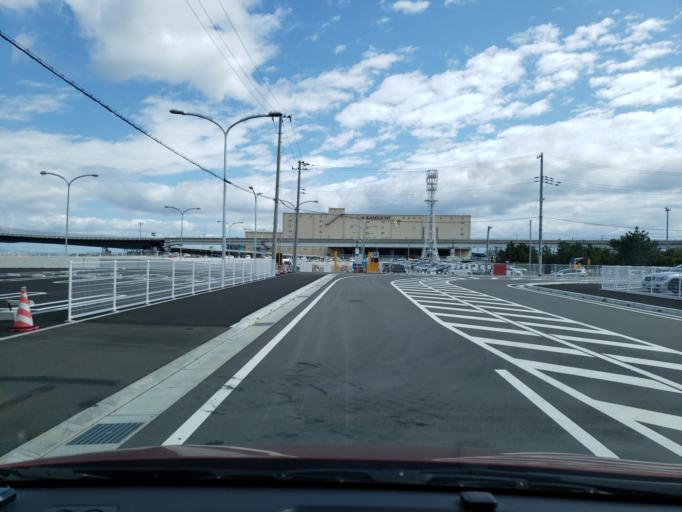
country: JP
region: Hyogo
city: Kobe
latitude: 34.6397
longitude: 135.2297
